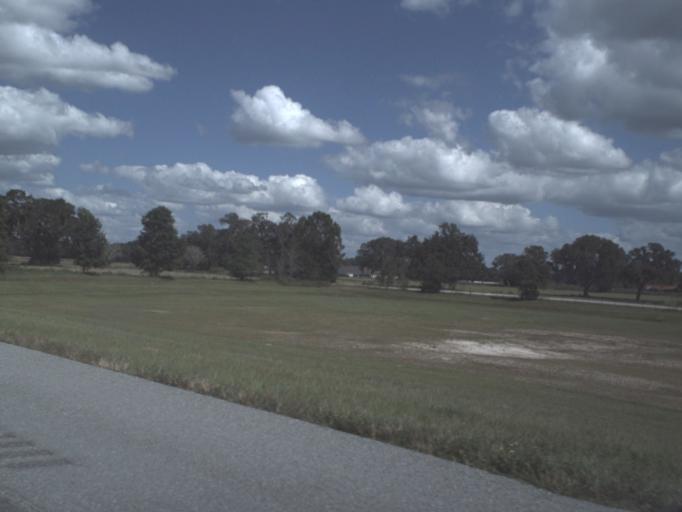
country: US
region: Florida
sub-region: Hernando County
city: Masaryktown
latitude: 28.4231
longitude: -82.4861
